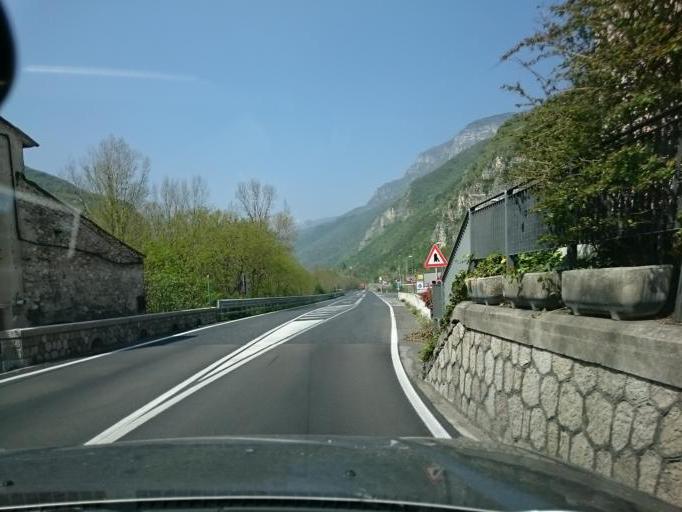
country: IT
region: Veneto
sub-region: Provincia di Vicenza
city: Campolongo sul Brenta
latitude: 45.8261
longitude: 11.7060
